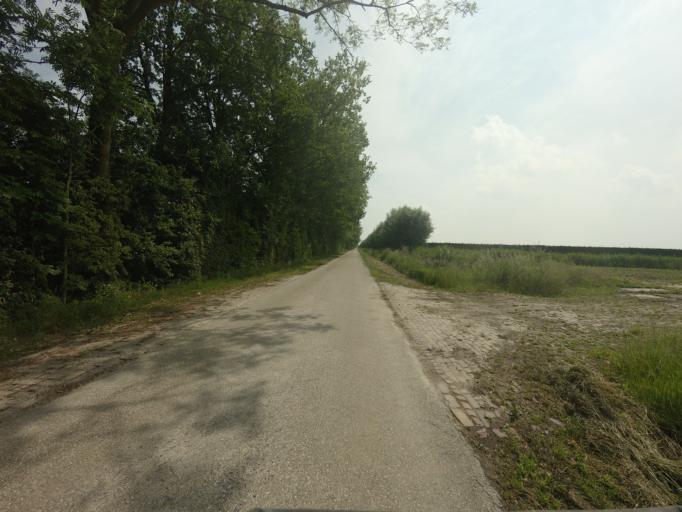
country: NL
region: Gelderland
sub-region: Gemeente Culemborg
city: Culemborg
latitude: 51.9975
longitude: 5.2141
